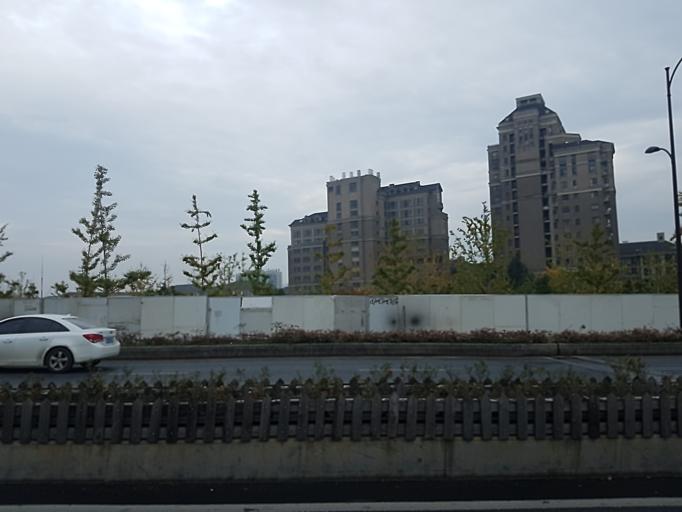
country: CN
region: Zhejiang Sheng
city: Jiangcun
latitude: 30.2965
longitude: 120.0801
